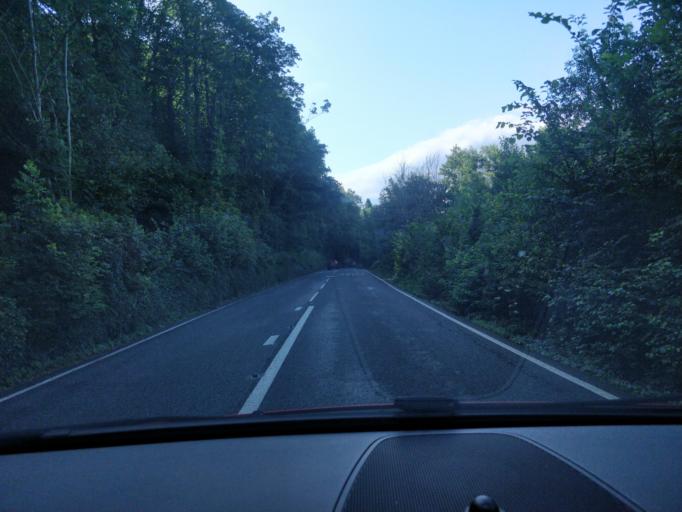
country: GB
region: Wales
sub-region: Conwy
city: Llanrwst
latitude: 53.1940
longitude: -3.8268
